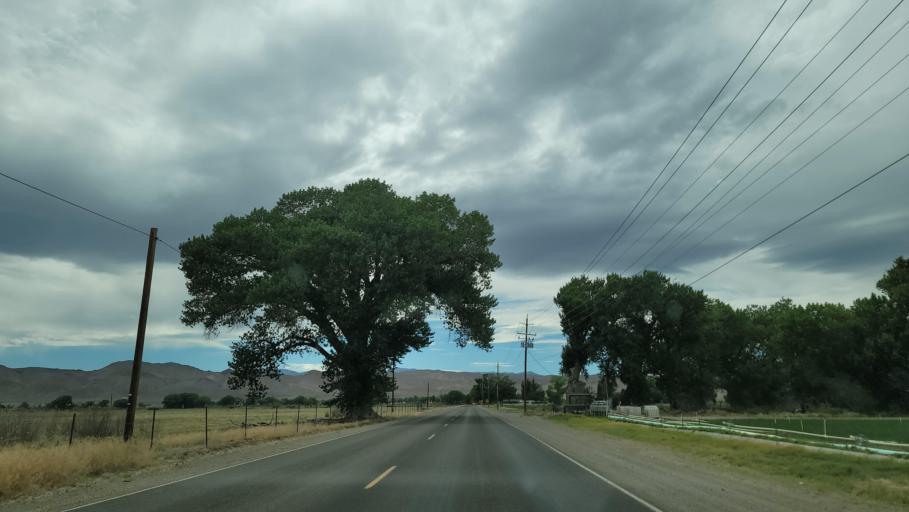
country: US
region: Nevada
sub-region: Lyon County
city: Yerington
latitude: 39.0481
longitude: -119.1755
